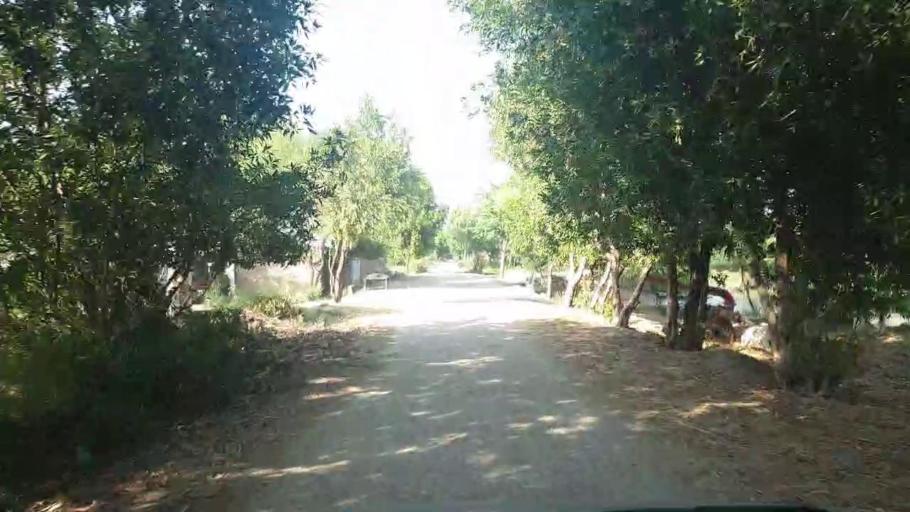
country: PK
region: Sindh
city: Badin
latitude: 24.6261
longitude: 68.8149
